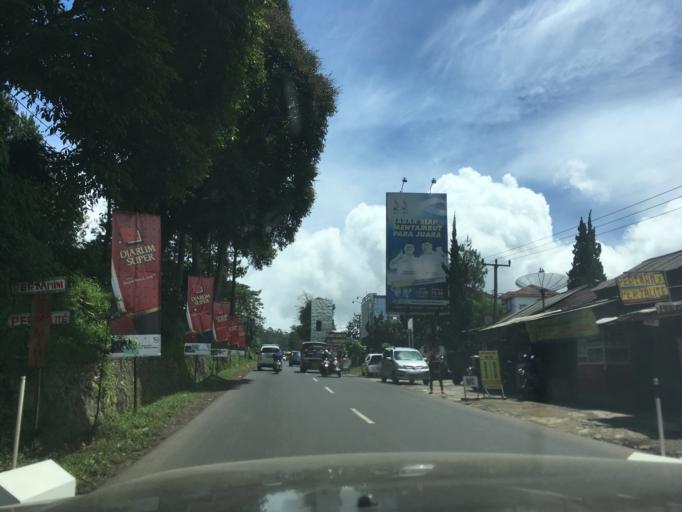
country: ID
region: West Java
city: Lembang
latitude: -6.8028
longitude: 107.6500
